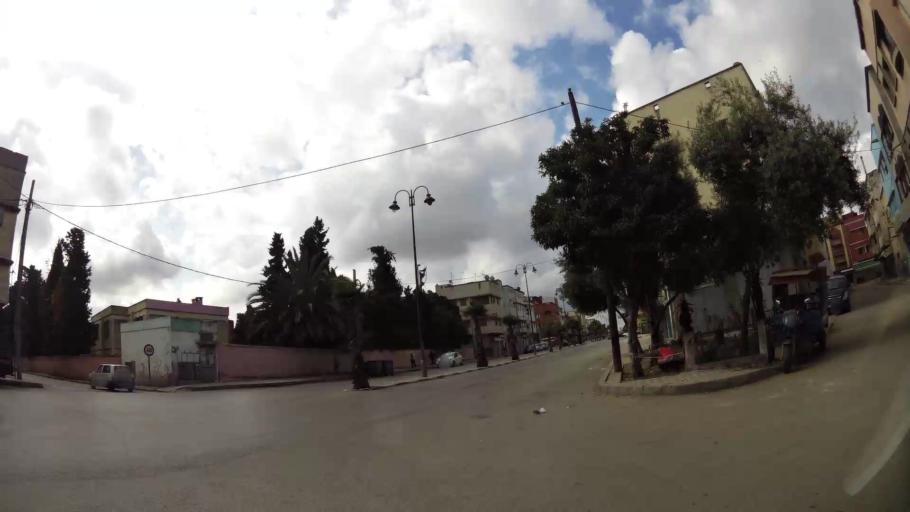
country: MA
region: Gharb-Chrarda-Beni Hssen
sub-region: Kenitra Province
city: Kenitra
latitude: 34.2668
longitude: -6.5614
